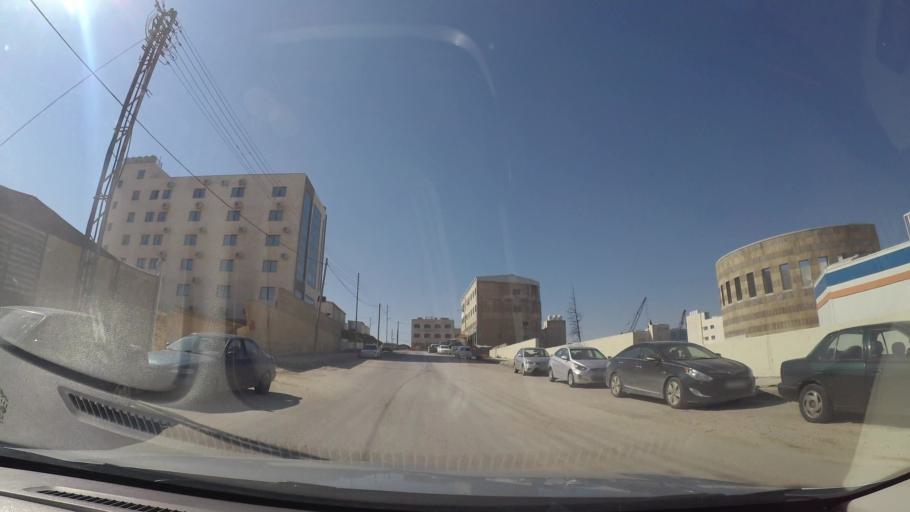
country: JO
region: Amman
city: Al Bunayyat ash Shamaliyah
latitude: 31.9152
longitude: 35.9096
